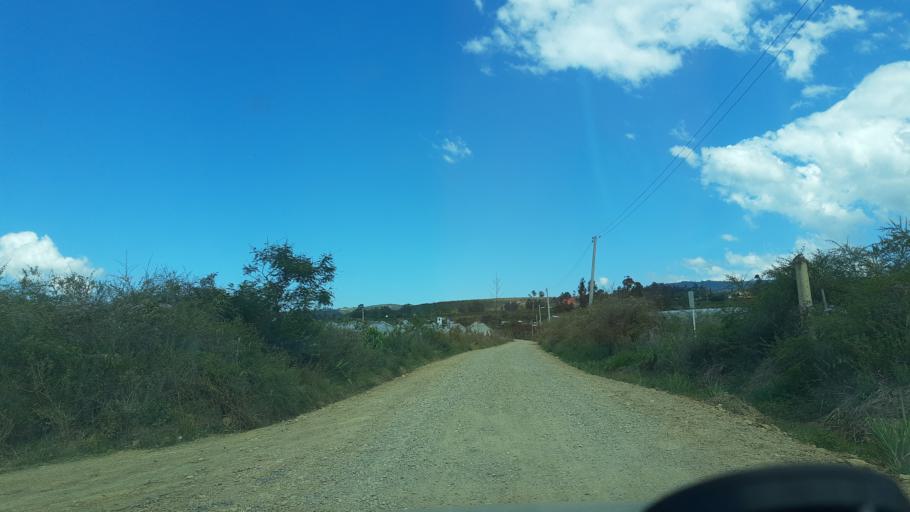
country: CO
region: Boyaca
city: Villa de Leiva
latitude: 5.6657
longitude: -73.5737
